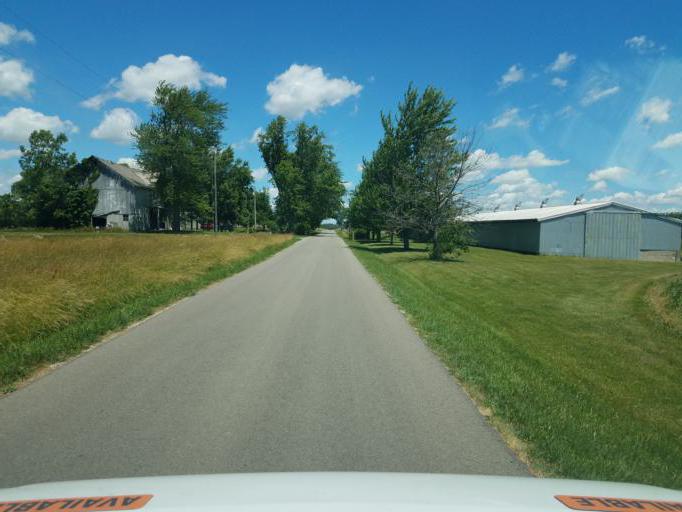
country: US
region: Ohio
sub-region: Crawford County
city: Galion
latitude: 40.7240
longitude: -82.8655
